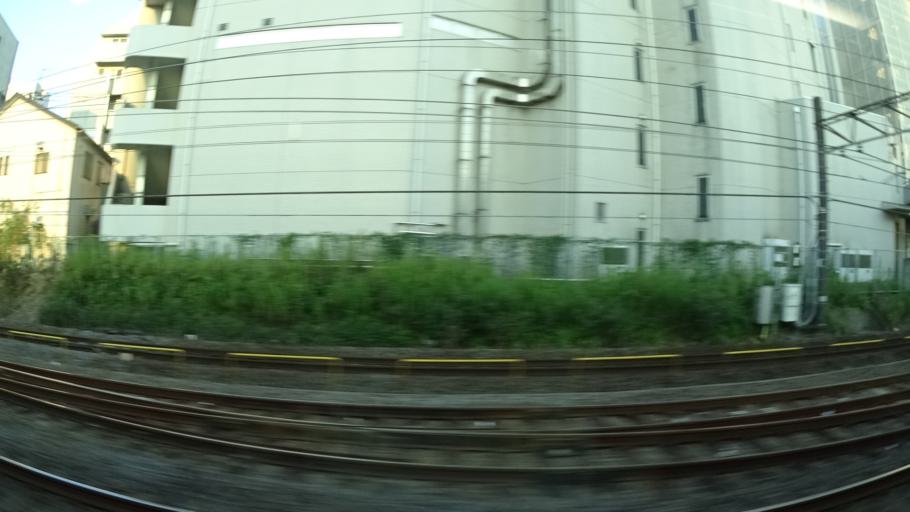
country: JP
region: Chiba
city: Kashiwa
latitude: 35.8643
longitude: 139.9724
